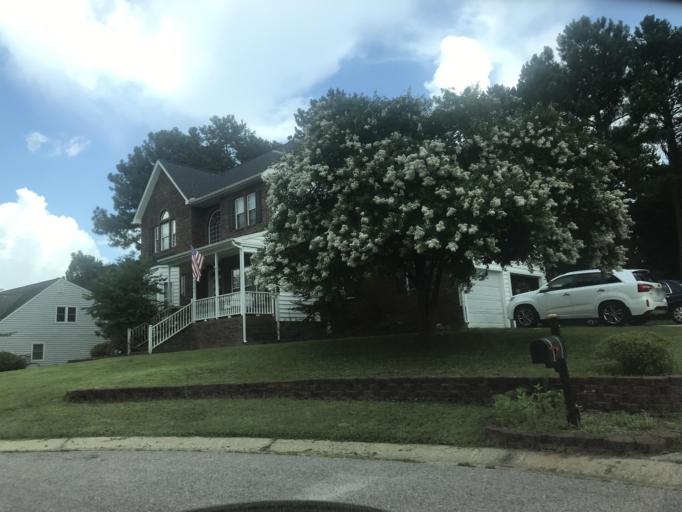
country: US
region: North Carolina
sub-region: Wake County
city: Knightdale
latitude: 35.8341
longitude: -78.5583
